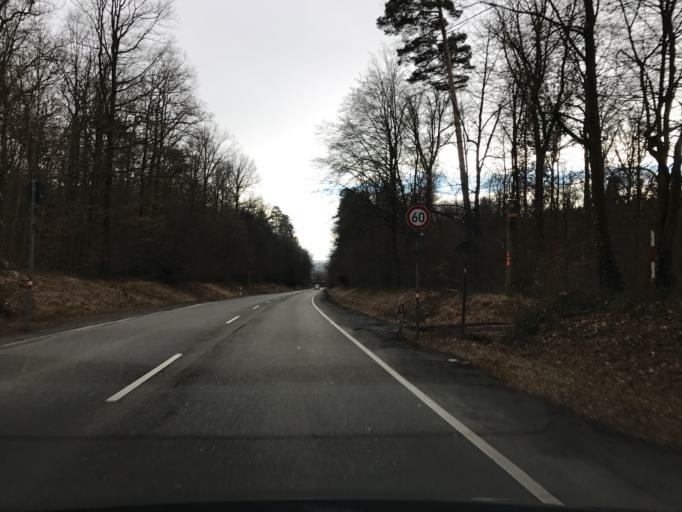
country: DE
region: Baden-Wuerttemberg
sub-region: Regierungsbezirk Stuttgart
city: Stuttgart-Ost
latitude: 48.7491
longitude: 9.1981
